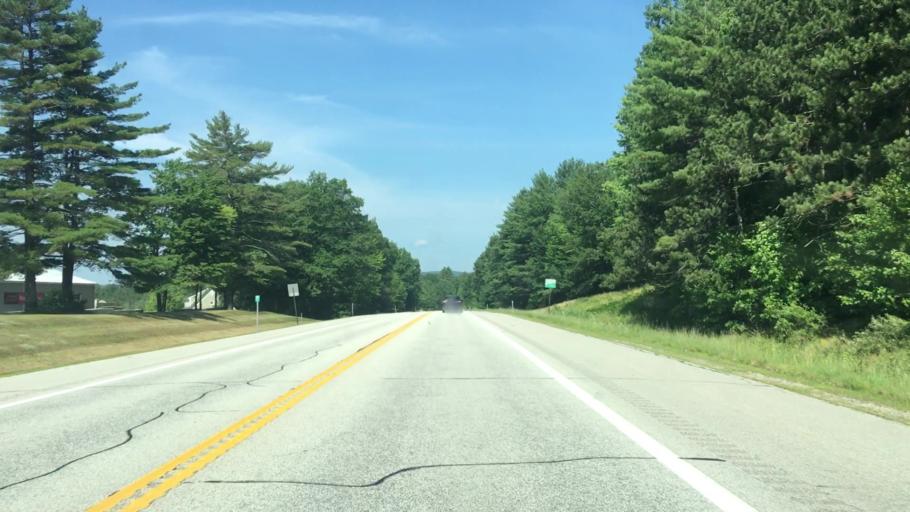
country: US
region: New Hampshire
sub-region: Merrimack County
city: Henniker
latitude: 43.1819
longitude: -71.7731
